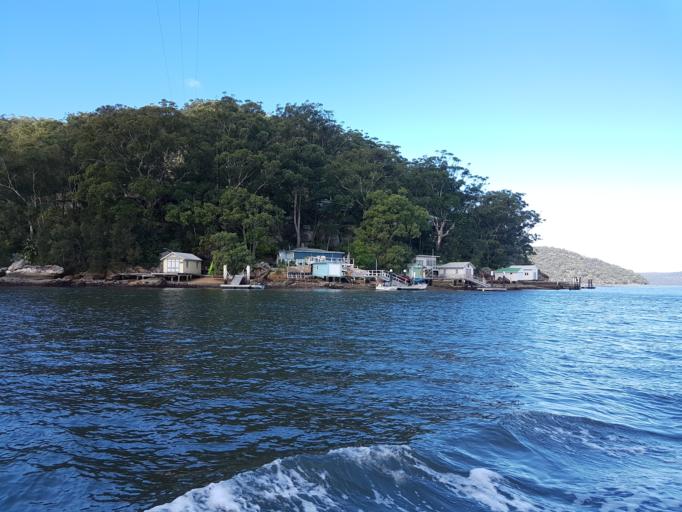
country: AU
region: New South Wales
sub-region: Gosford Shire
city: Umina
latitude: -33.5402
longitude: 151.2338
